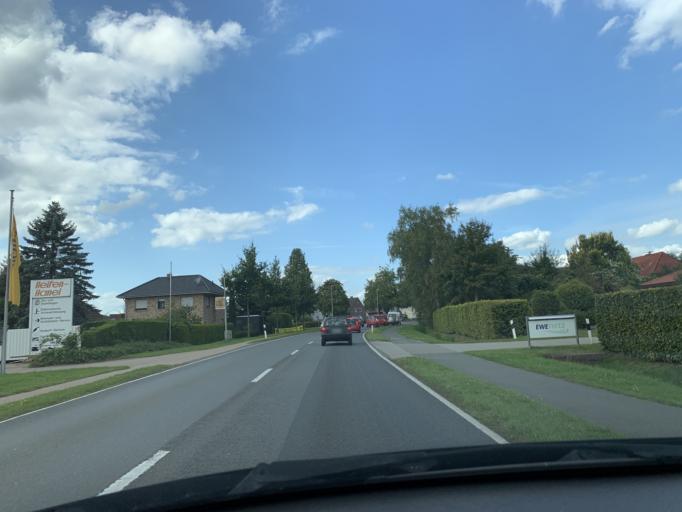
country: DE
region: Lower Saxony
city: Bad Zwischenahn
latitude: 53.1744
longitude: 7.9959
